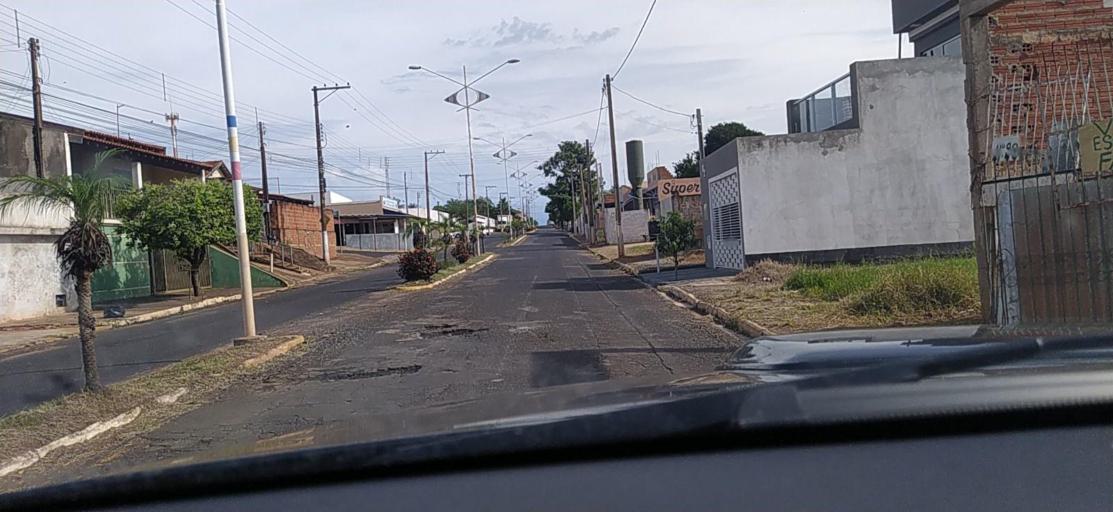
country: BR
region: Sao Paulo
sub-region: Catanduva
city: Catanduva
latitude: -21.0624
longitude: -49.0628
